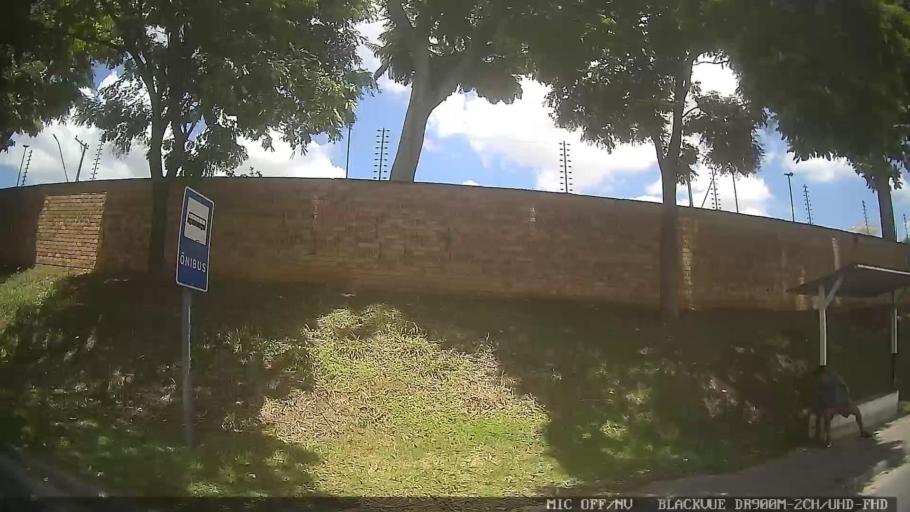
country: BR
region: Sao Paulo
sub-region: Jacarei
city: Jacarei
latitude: -23.3017
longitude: -45.9478
